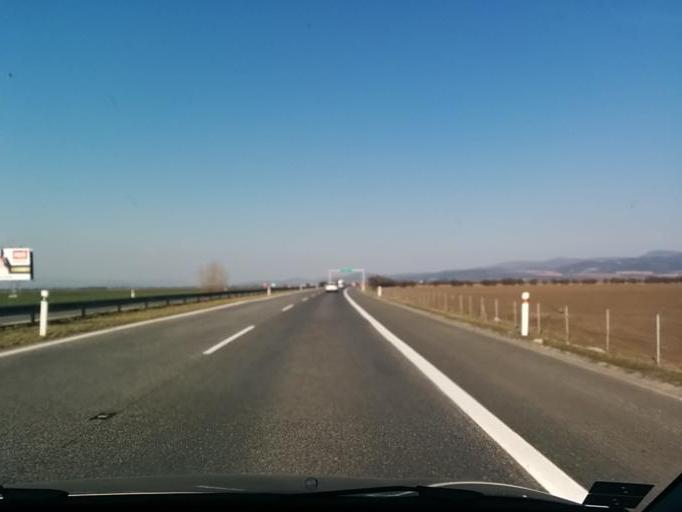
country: SK
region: Trnavsky
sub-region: Okres Trnava
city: Piestany
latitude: 48.6370
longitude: 17.8125
